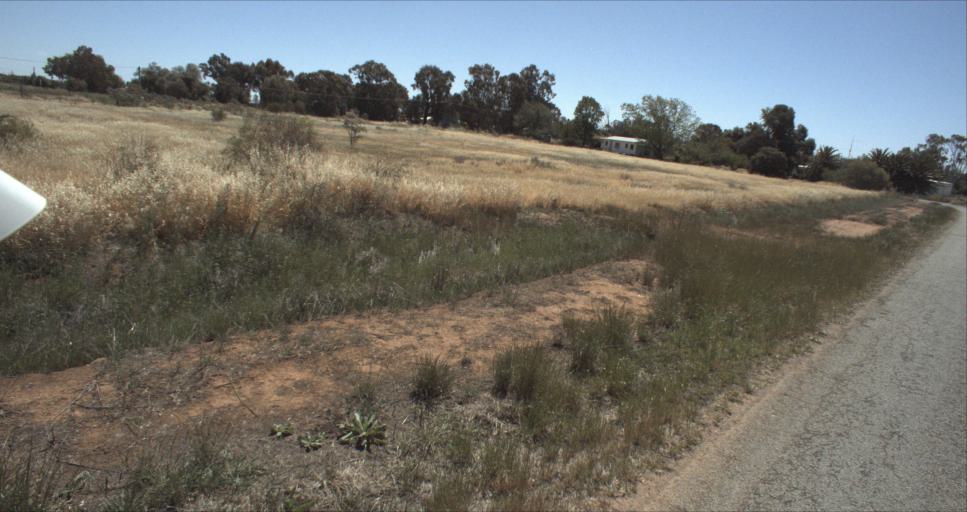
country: AU
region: New South Wales
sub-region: Leeton
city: Leeton
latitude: -34.5272
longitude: 146.3333
